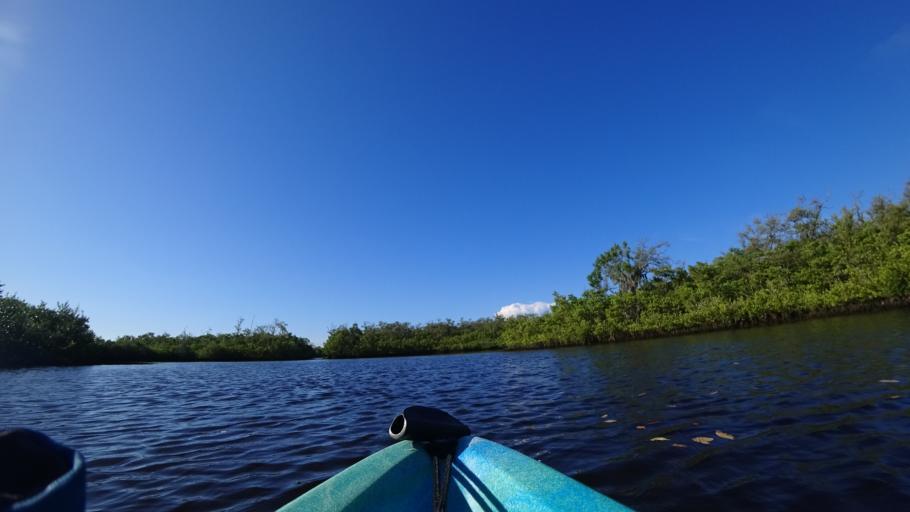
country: US
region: Florida
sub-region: Manatee County
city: Holmes Beach
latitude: 27.5094
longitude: -82.6715
